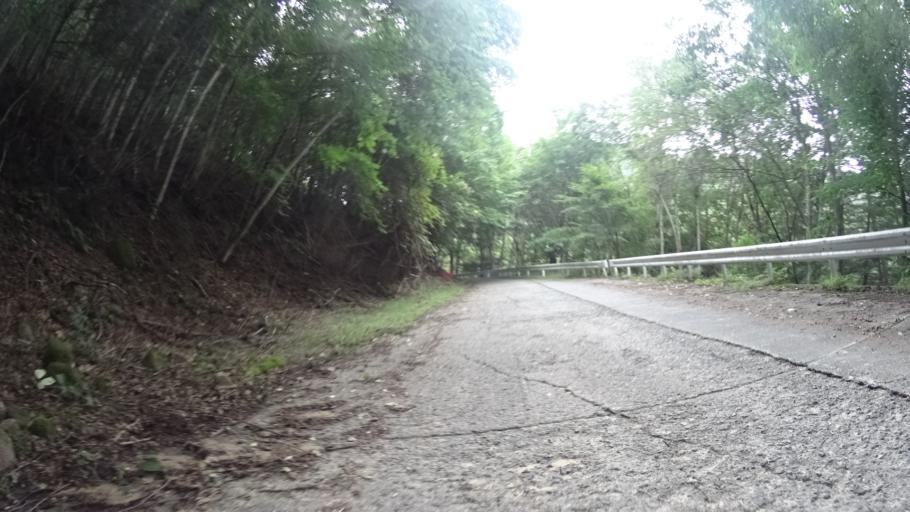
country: JP
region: Yamanashi
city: Kofu-shi
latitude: 35.8506
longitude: 138.5771
